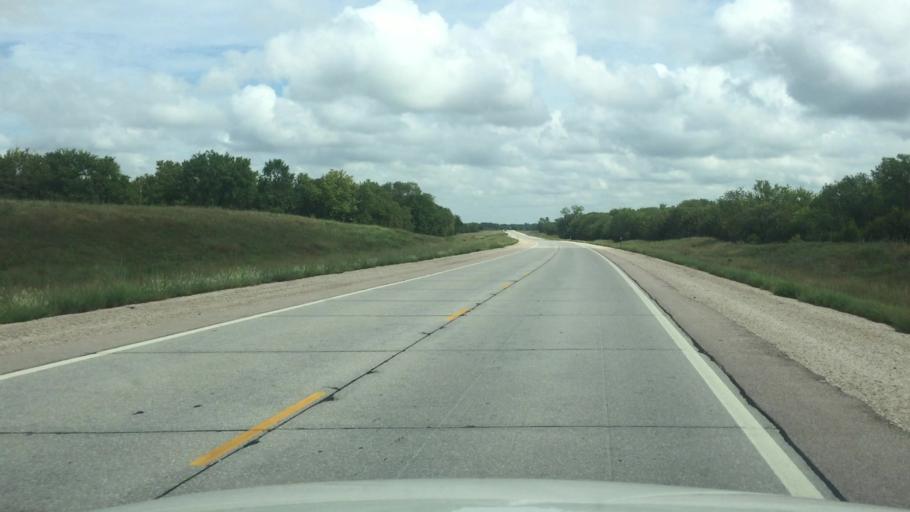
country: US
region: Kansas
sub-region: Allen County
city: Iola
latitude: 37.8987
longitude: -95.3831
